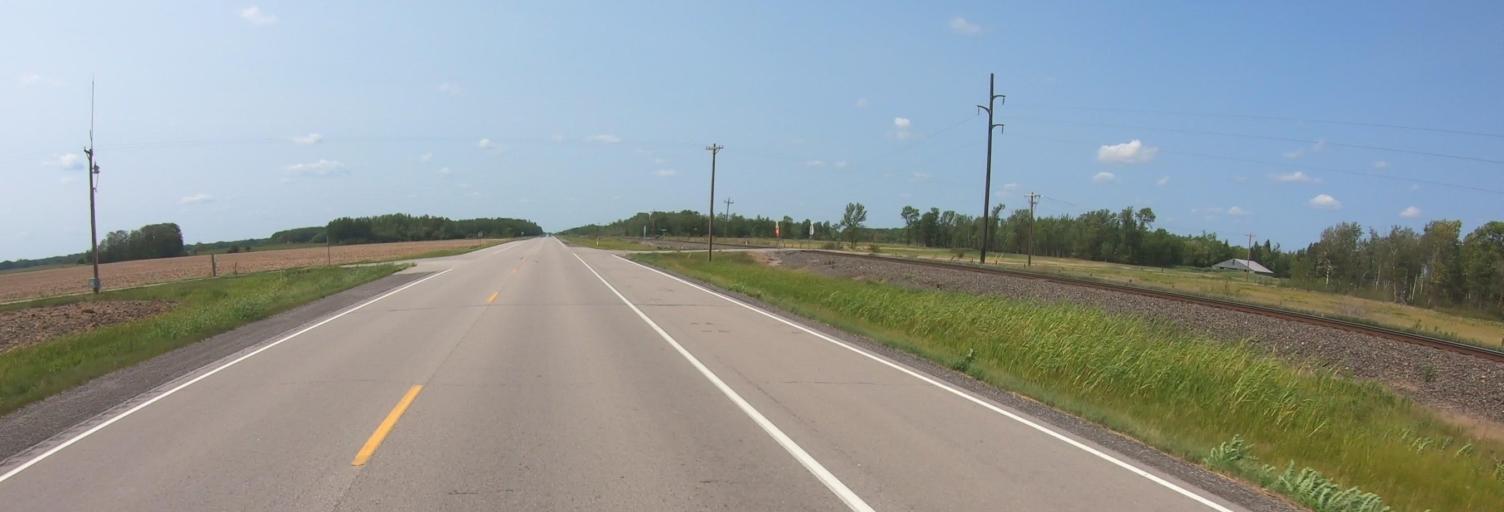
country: US
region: Minnesota
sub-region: Lake of the Woods County
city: Baudette
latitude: 48.7224
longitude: -94.7606
